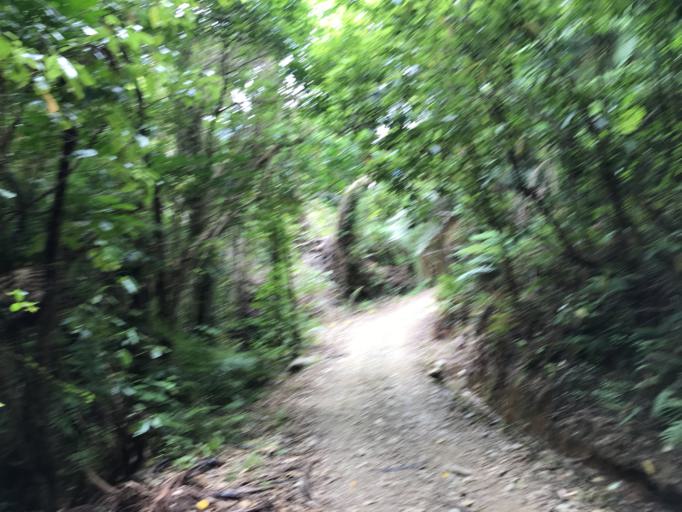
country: NZ
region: Marlborough
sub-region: Marlborough District
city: Picton
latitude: -41.0949
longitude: 174.1884
